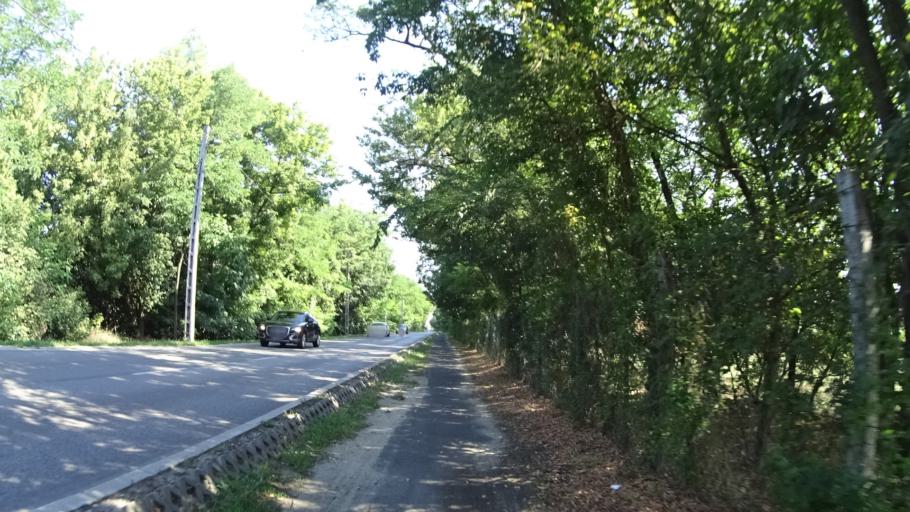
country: HU
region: Pest
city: Dunakeszi
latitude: 47.6173
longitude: 19.1331
